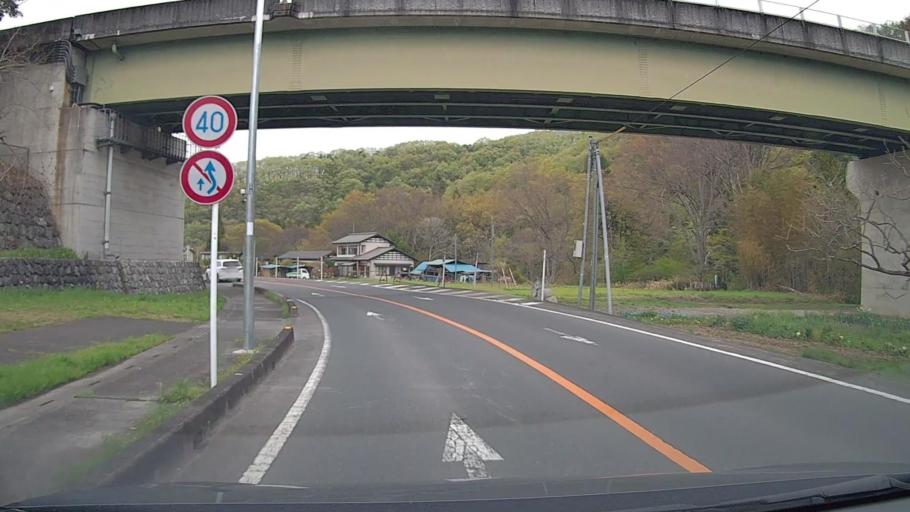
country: JP
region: Saitama
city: Yorii
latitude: 36.0748
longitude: 139.1191
